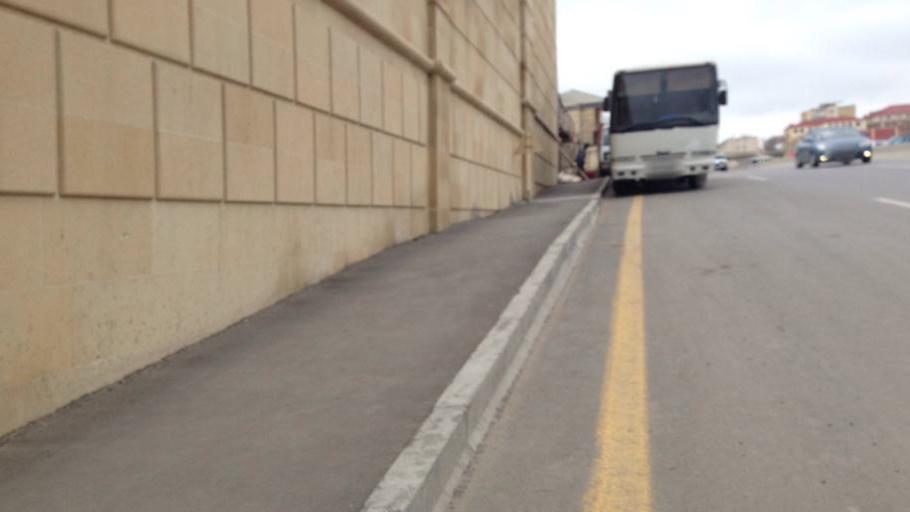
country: AZ
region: Baki
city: Bilajari
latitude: 40.4090
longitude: 49.8282
